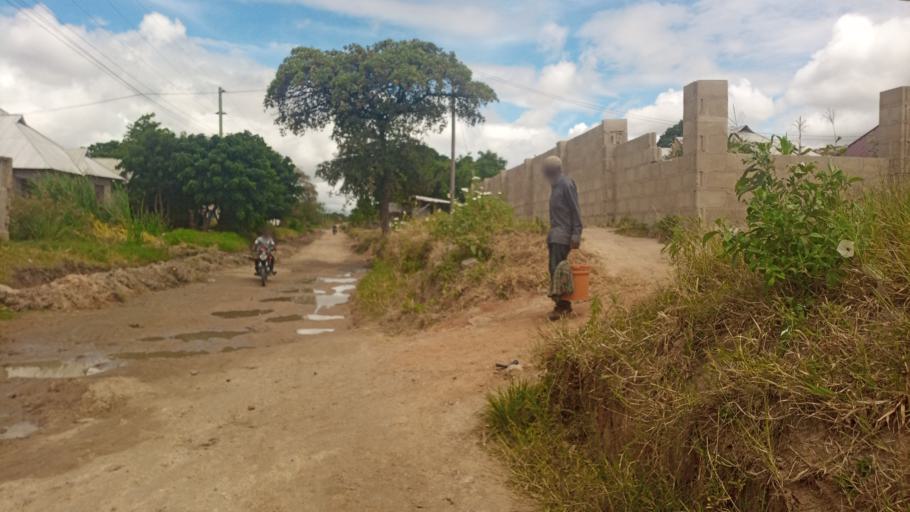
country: TZ
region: Dodoma
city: Dodoma
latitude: -6.1886
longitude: 35.7239
